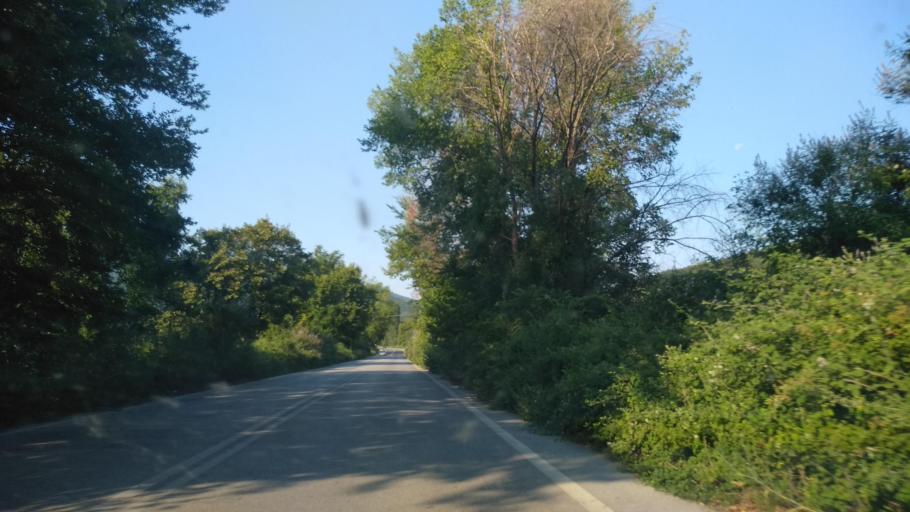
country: GR
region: Central Macedonia
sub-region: Nomos Thessalonikis
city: Stavros
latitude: 40.6831
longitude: 23.6760
